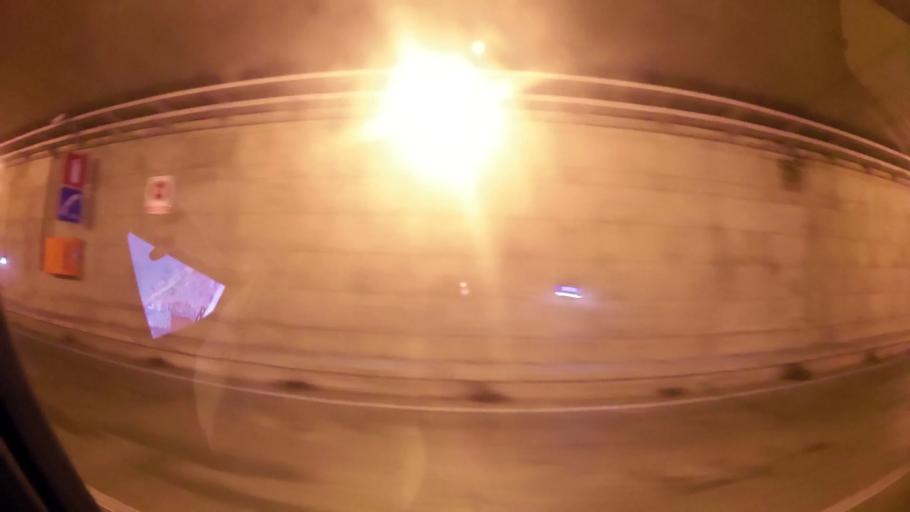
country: CO
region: Bolivar
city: Cartagena
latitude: 10.4463
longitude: -75.5230
